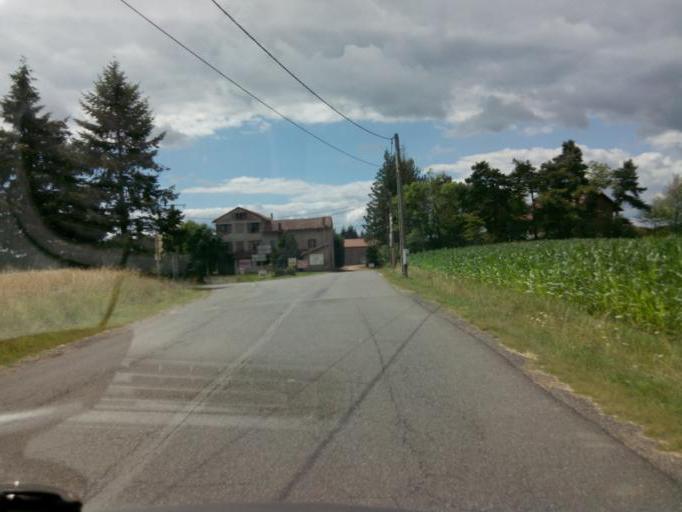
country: FR
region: Rhone-Alpes
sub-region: Departement de la Loire
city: Usson-en-Forez
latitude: 45.3760
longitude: 3.9955
